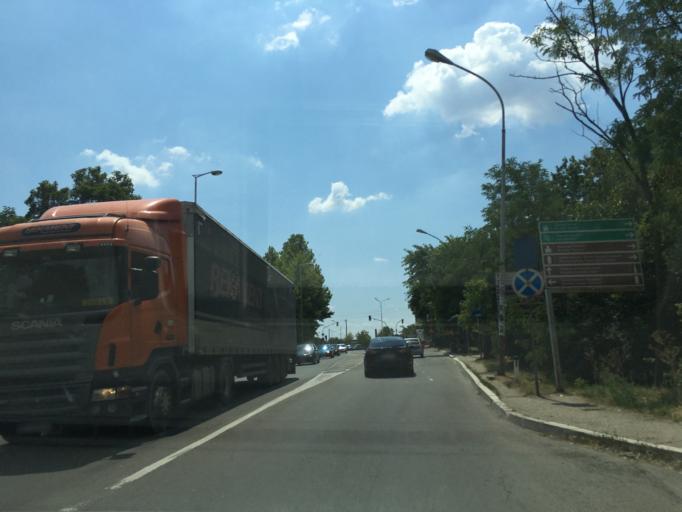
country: RS
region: Central Serbia
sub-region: Belgrade
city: Mladenovac
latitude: 44.4485
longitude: 20.6866
